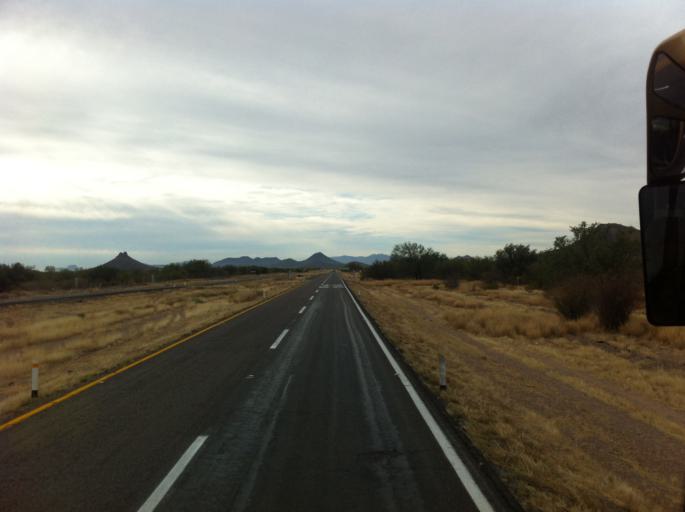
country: MX
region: Sonora
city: Hermosillo
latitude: 28.9273
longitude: -110.9532
